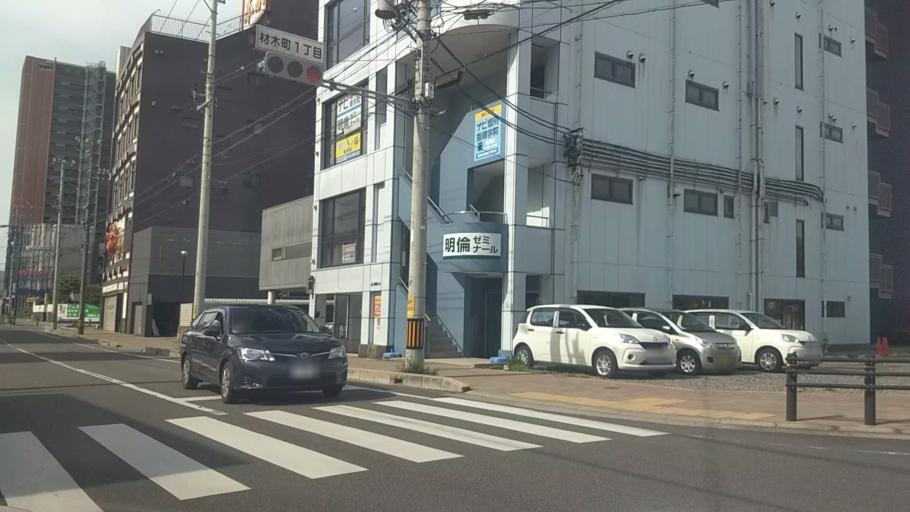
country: JP
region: Aichi
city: Okazaki
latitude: 34.9601
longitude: 137.1621
